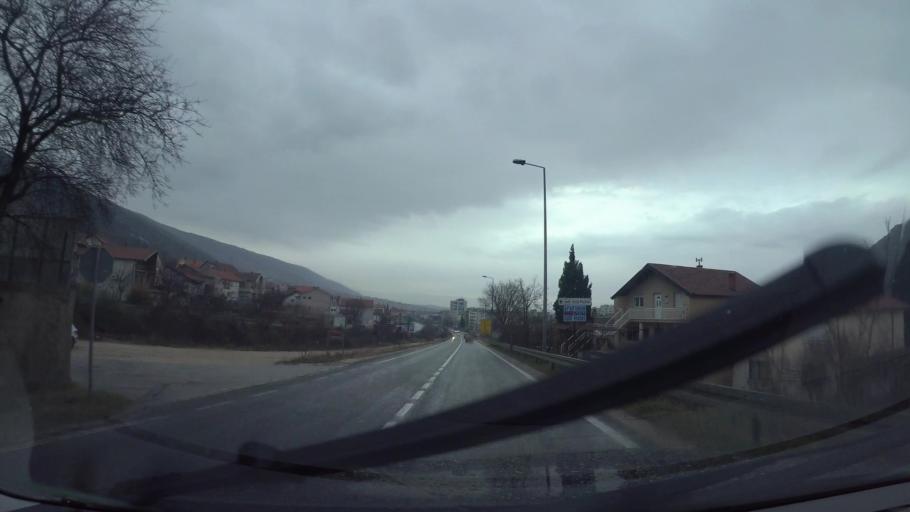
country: BA
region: Federation of Bosnia and Herzegovina
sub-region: Hercegovacko-Bosanski Kanton
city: Mostar
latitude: 43.3314
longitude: 17.8209
